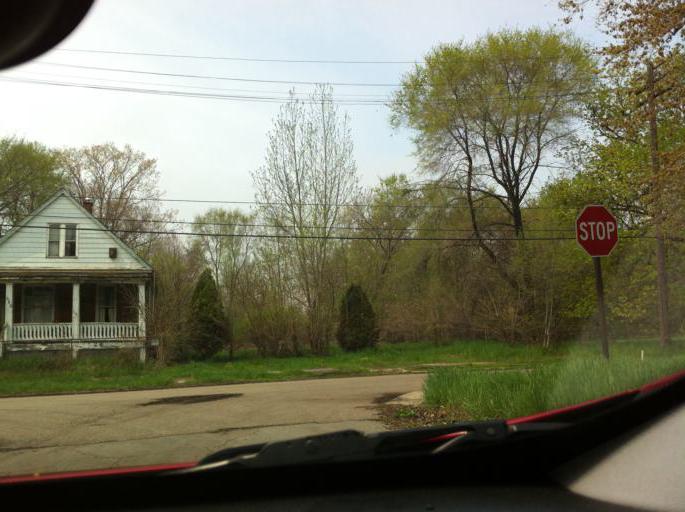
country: US
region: Michigan
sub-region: Wayne County
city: River Rouge
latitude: 42.3033
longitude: -83.0960
